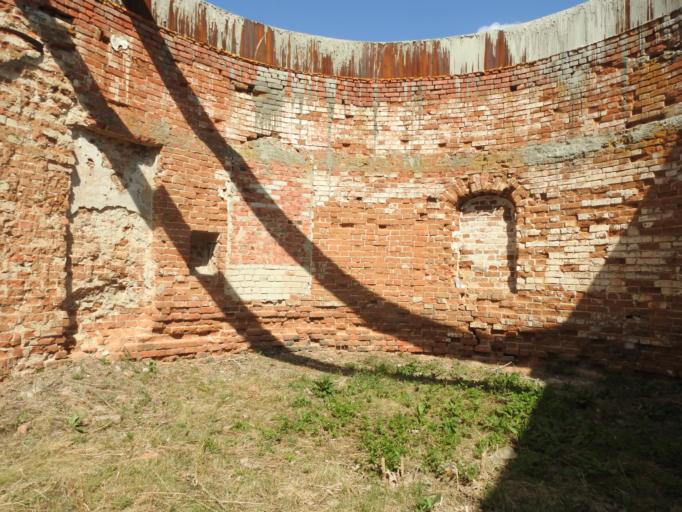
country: RU
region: Volgograd
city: Zhirnovsk
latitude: 51.2160
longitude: 44.9560
